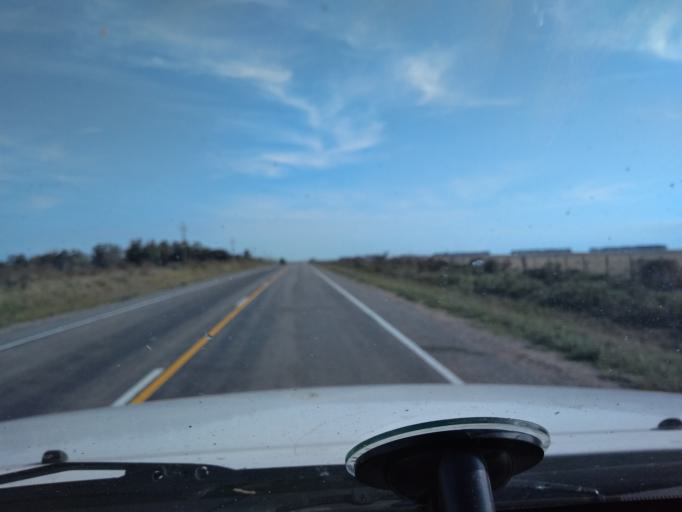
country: UY
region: Florida
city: Casupa
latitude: -34.0182
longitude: -55.8549
